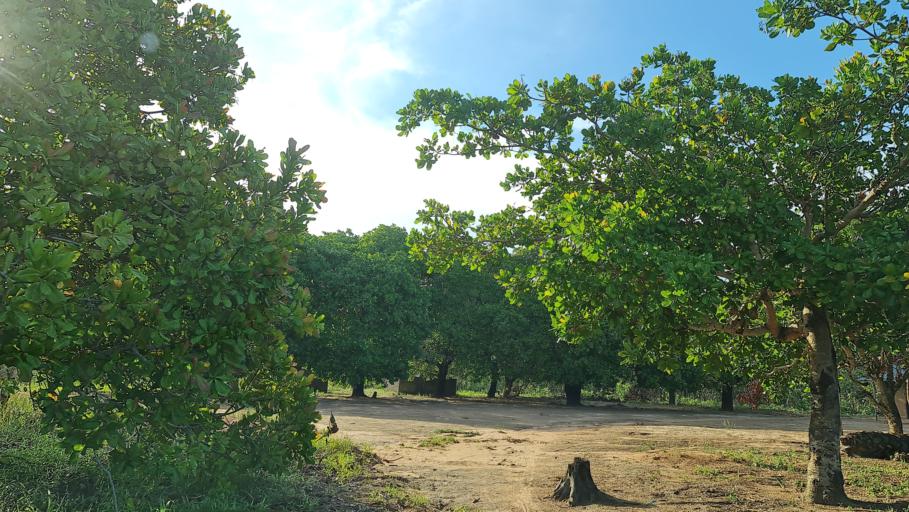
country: MZ
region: Zambezia
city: Quelimane
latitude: -17.1915
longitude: 37.4128
